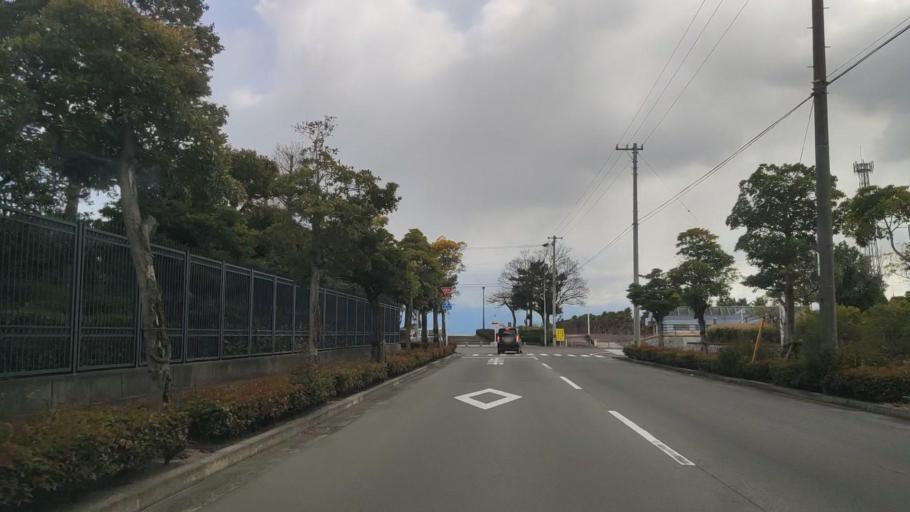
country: JP
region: Ehime
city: Saijo
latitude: 34.0466
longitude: 133.0287
